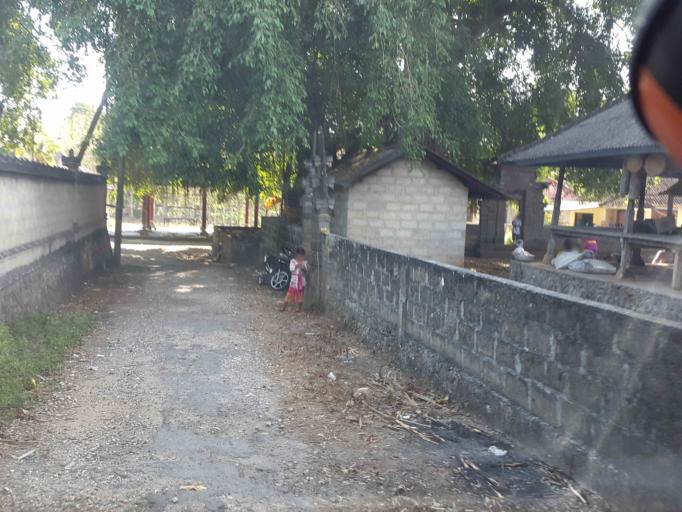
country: ID
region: Bali
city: Pondokkaha Kelod
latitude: -8.7310
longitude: 115.4712
